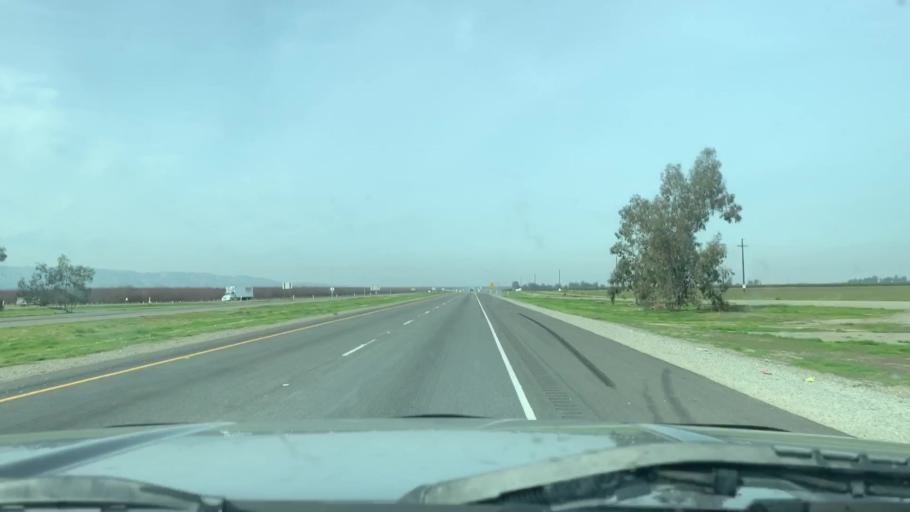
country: US
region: California
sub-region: Fresno County
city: Mendota
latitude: 36.6399
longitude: -120.6229
